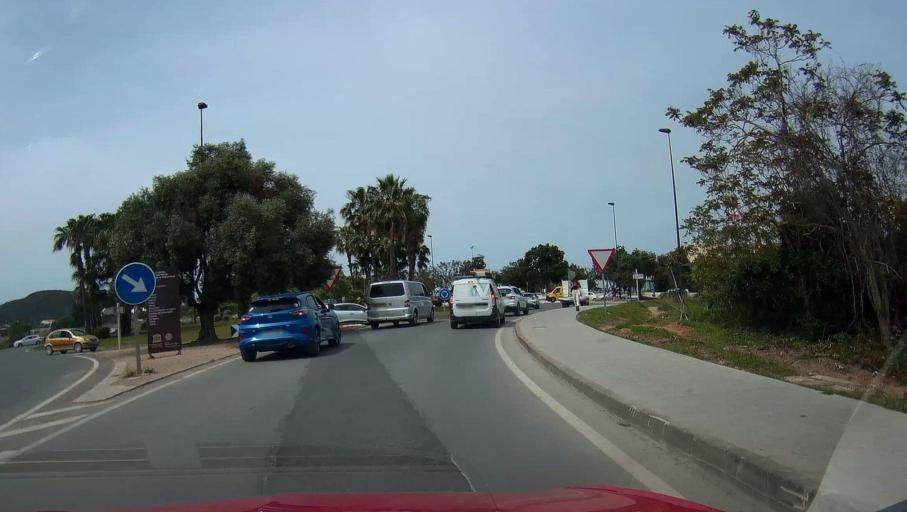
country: ES
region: Balearic Islands
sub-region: Illes Balears
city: Ibiza
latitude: 38.9154
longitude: 1.4286
